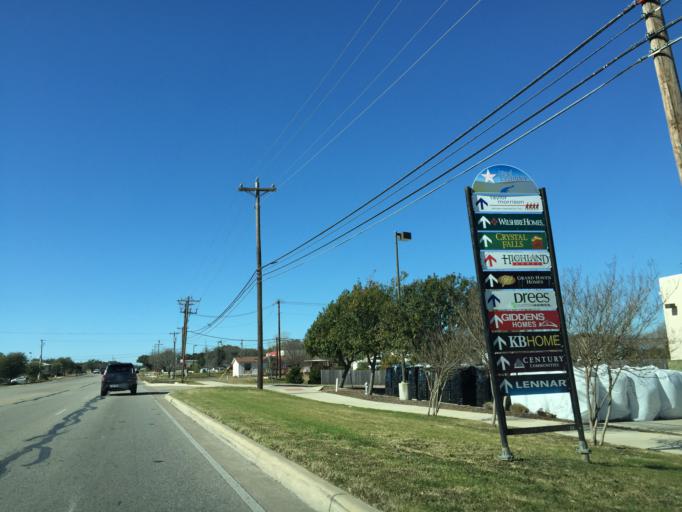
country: US
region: Texas
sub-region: Williamson County
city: Leander
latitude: 30.5574
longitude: -97.8461
